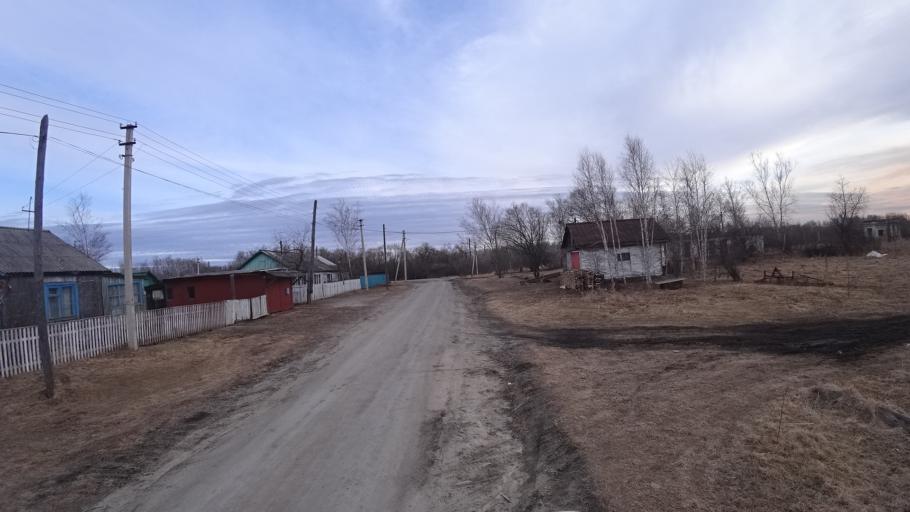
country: RU
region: Amur
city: Bureya
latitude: 50.0208
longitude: 129.7779
